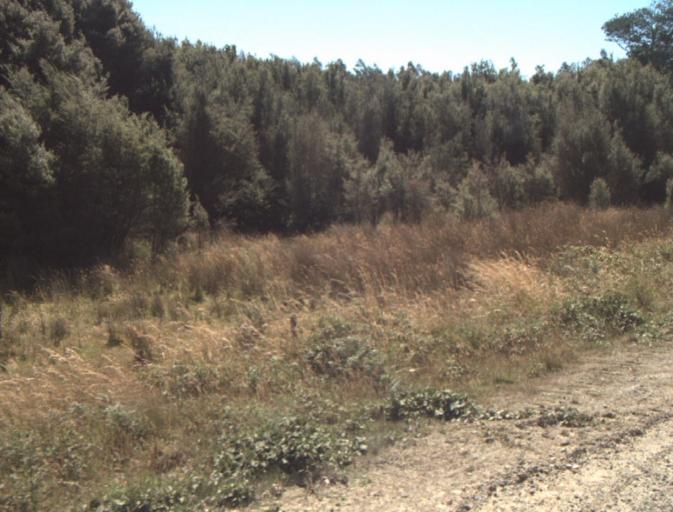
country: AU
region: Tasmania
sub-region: Dorset
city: Scottsdale
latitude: -41.3404
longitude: 147.4308
